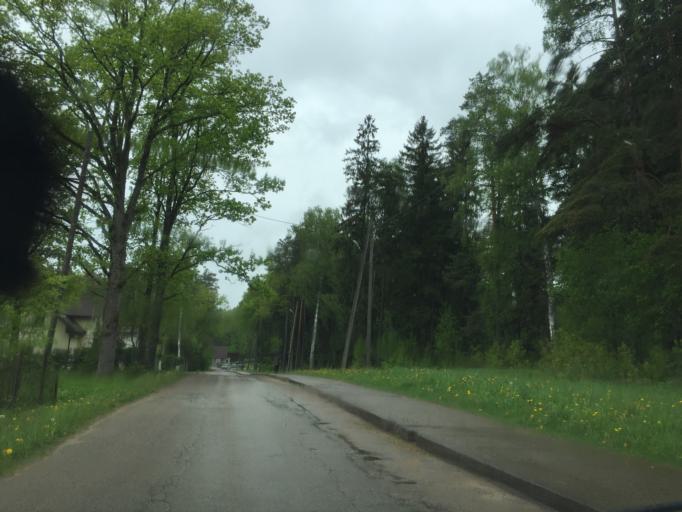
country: LV
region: Lielvarde
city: Lielvarde
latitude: 56.7291
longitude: 24.8075
